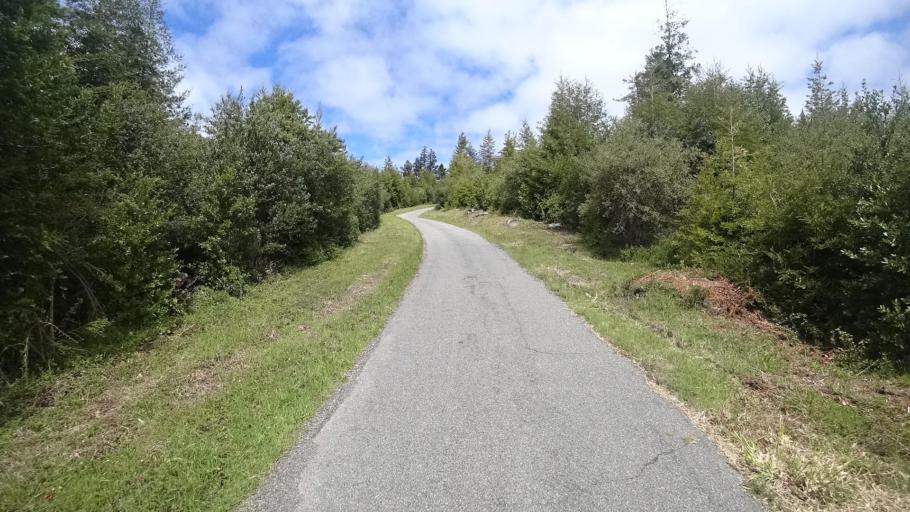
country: US
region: California
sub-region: Humboldt County
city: Blue Lake
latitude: 40.7861
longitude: -123.9653
